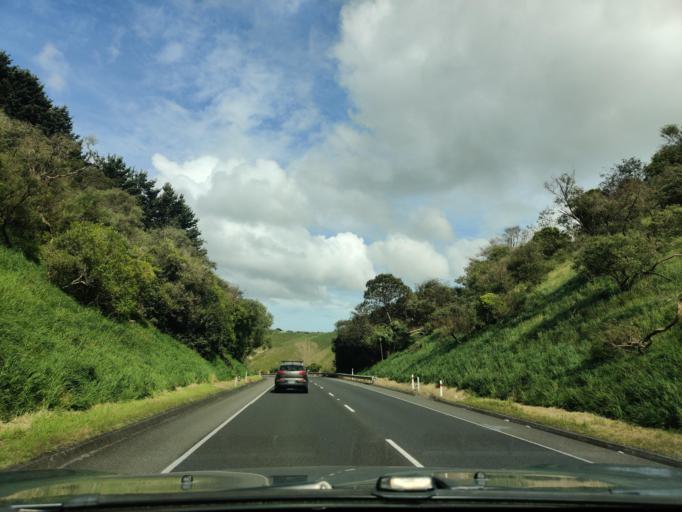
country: NZ
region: Manawatu-Wanganui
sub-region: Wanganui District
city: Wanganui
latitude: -39.8581
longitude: 174.9598
